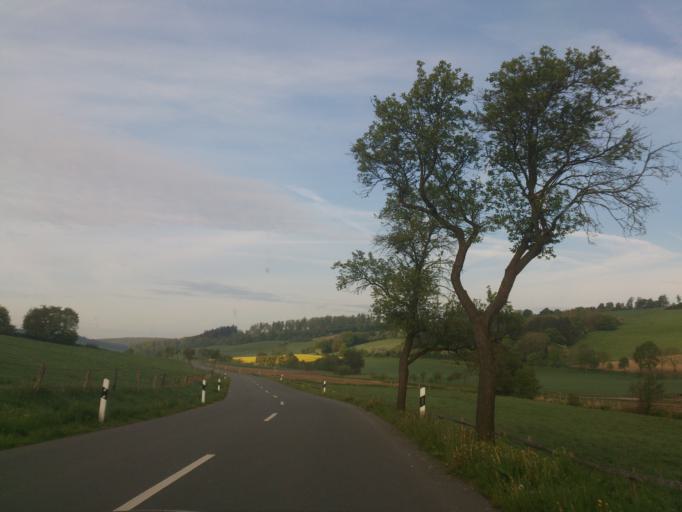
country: DE
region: North Rhine-Westphalia
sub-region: Regierungsbezirk Detmold
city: Altenbeken
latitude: 51.7103
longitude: 8.9066
